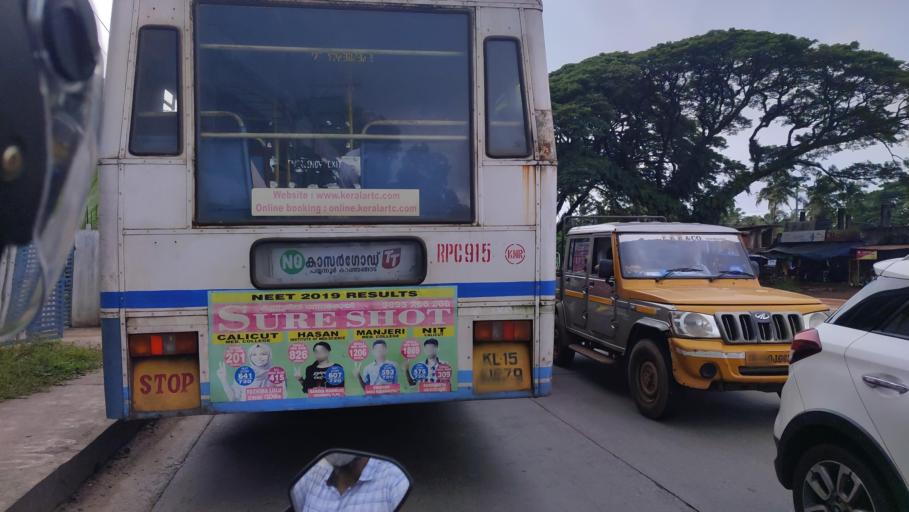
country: IN
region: Kerala
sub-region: Kasaragod District
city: Nileshwar
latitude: 12.2435
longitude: 75.1425
